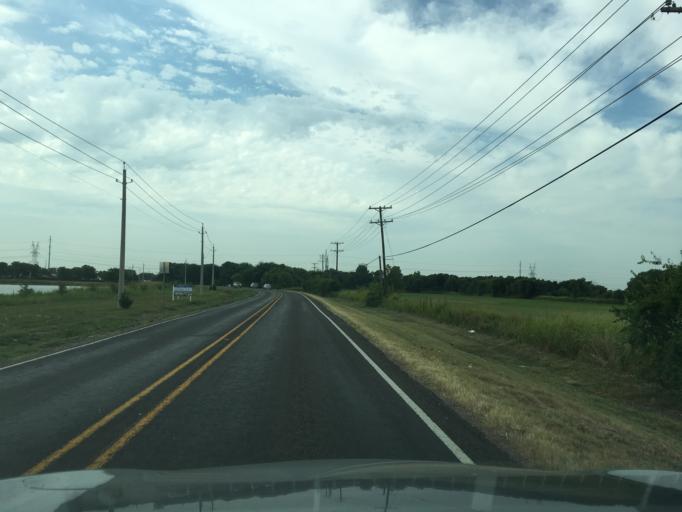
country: US
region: Texas
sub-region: Collin County
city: Parker
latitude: 33.0669
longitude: -96.6204
